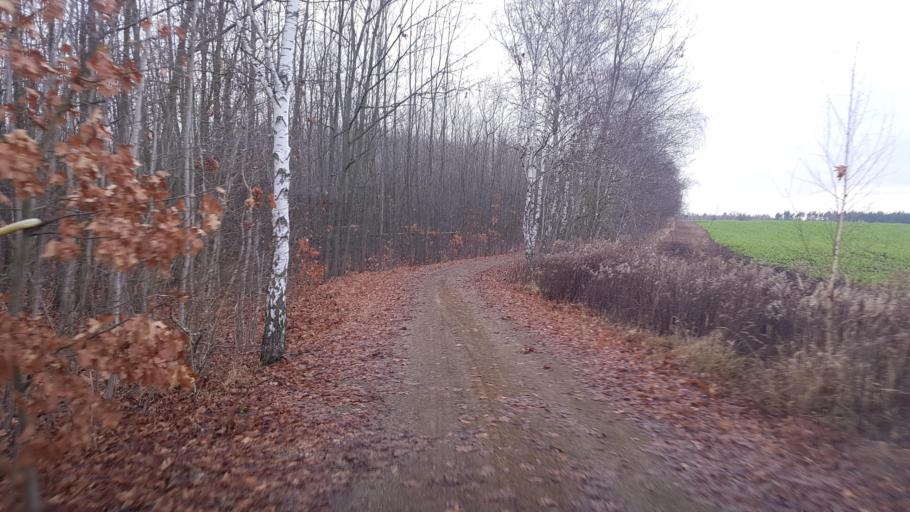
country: DE
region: Brandenburg
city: Lauchhammer
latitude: 51.5216
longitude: 13.6986
